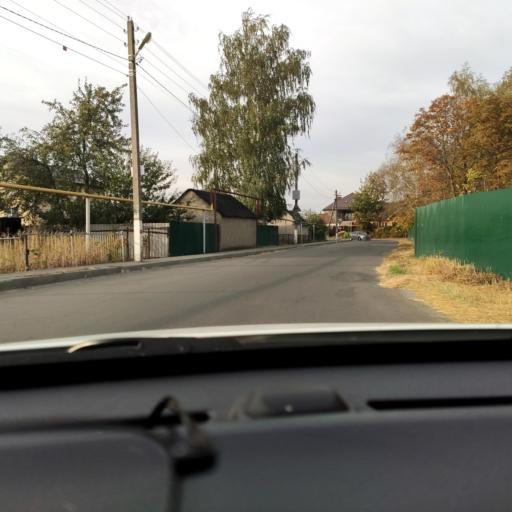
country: RU
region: Voronezj
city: Somovo
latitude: 51.6878
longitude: 39.3205
